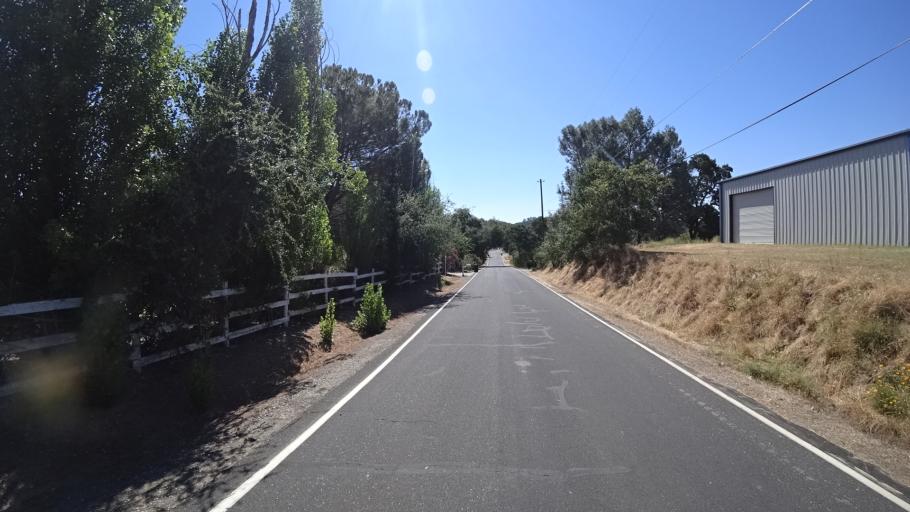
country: US
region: California
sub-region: Calaveras County
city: Rancho Calaveras
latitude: 38.1438
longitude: -120.8662
